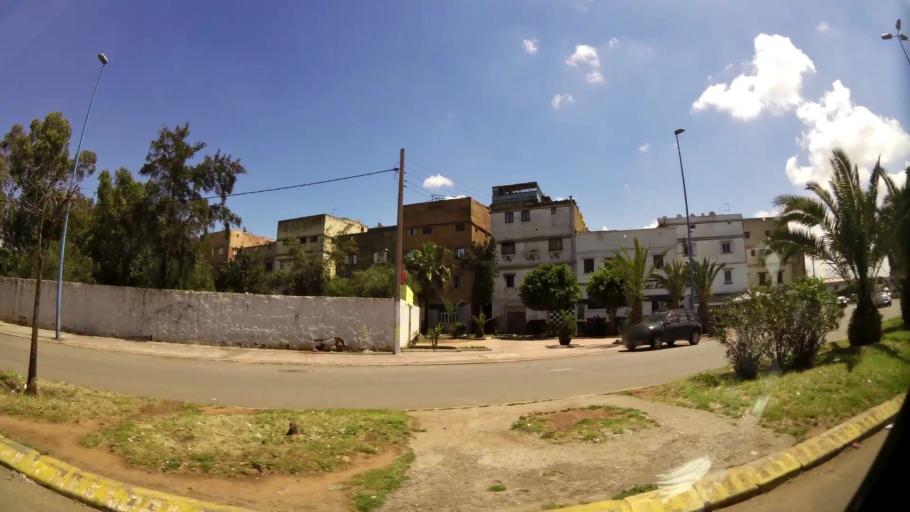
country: MA
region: Grand Casablanca
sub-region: Casablanca
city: Casablanca
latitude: 33.5622
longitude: -7.5764
